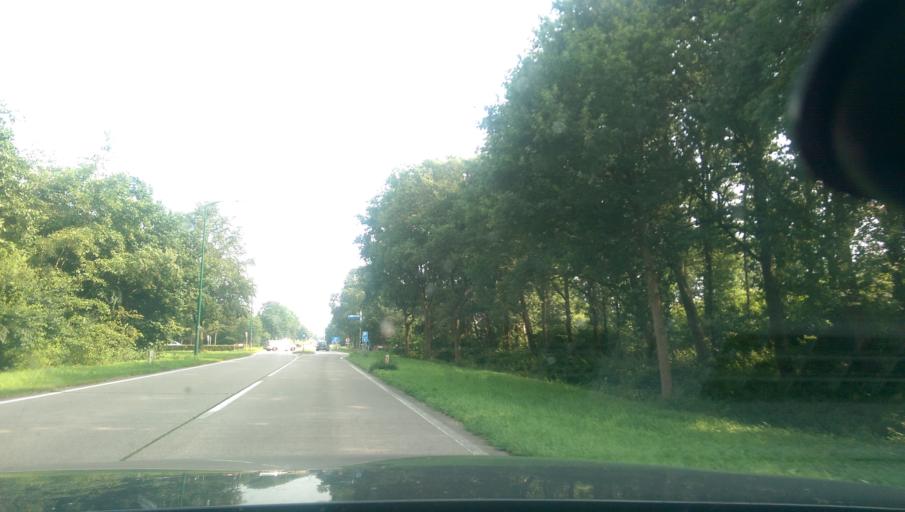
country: NL
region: North Brabant
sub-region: Gemeente Eersel
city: Eersel
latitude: 51.3775
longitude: 5.3162
